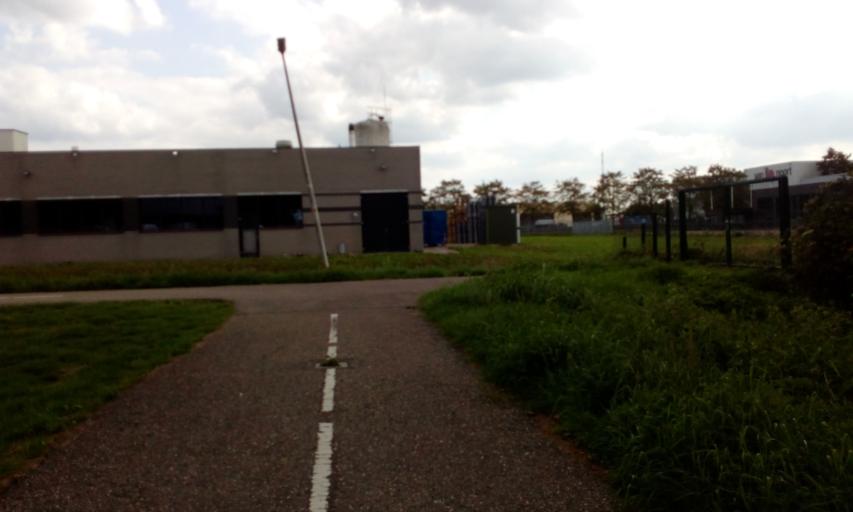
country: NL
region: South Holland
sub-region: Gemeente Waddinxveen
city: Waddinxveen
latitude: 52.0303
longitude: 4.6498
